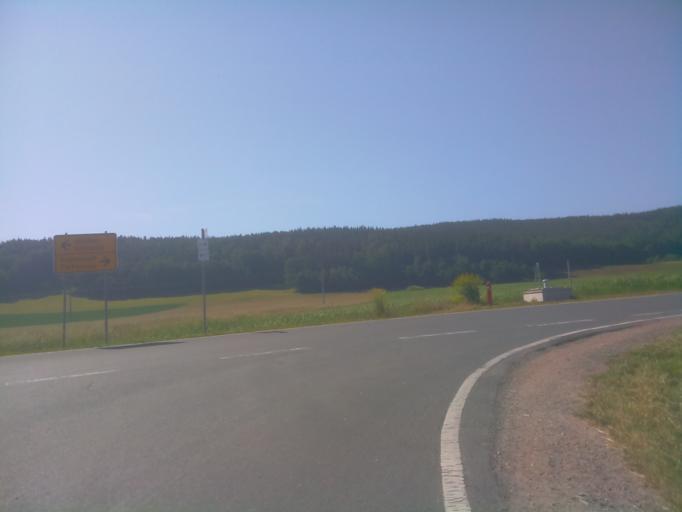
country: DE
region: Thuringia
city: Rudolstadt
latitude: 50.7171
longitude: 11.3999
